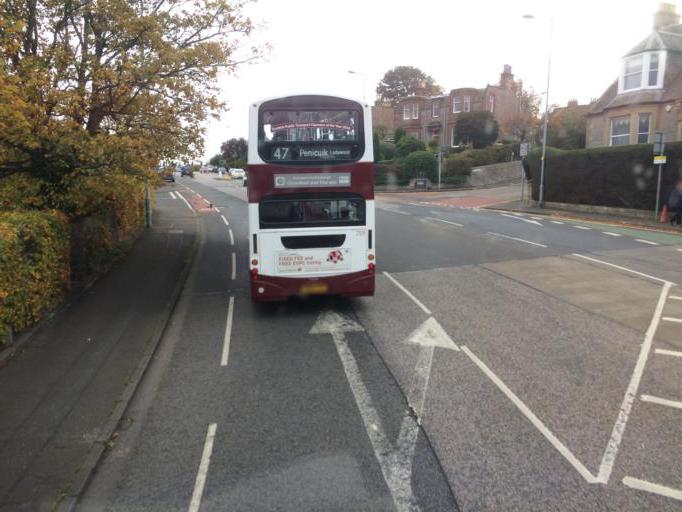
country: GB
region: Scotland
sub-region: Midlothian
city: Loanhead
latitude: 55.9165
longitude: -3.1675
